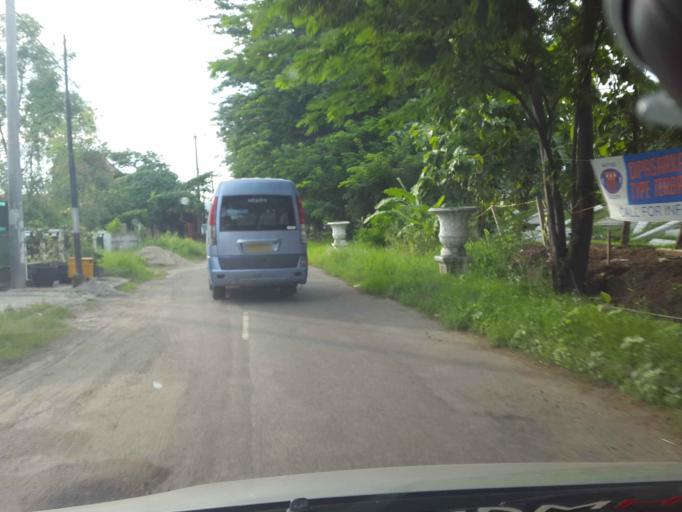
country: ID
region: Banten
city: Pangarengan
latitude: -6.0002
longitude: 106.0602
